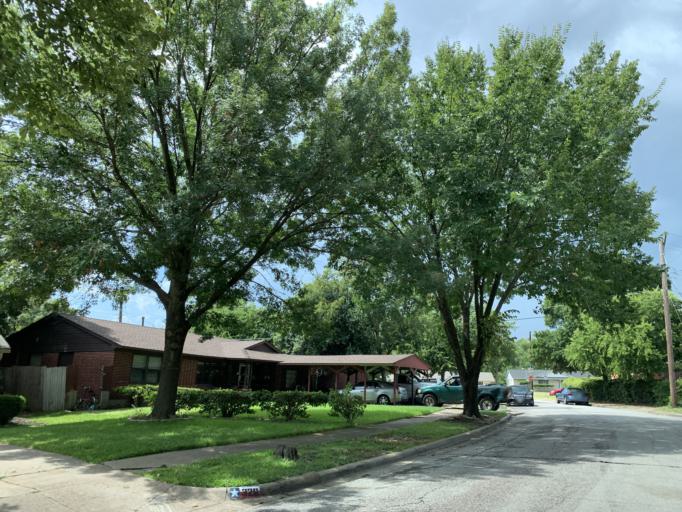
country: US
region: Texas
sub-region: Dallas County
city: DeSoto
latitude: 32.6660
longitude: -96.8278
